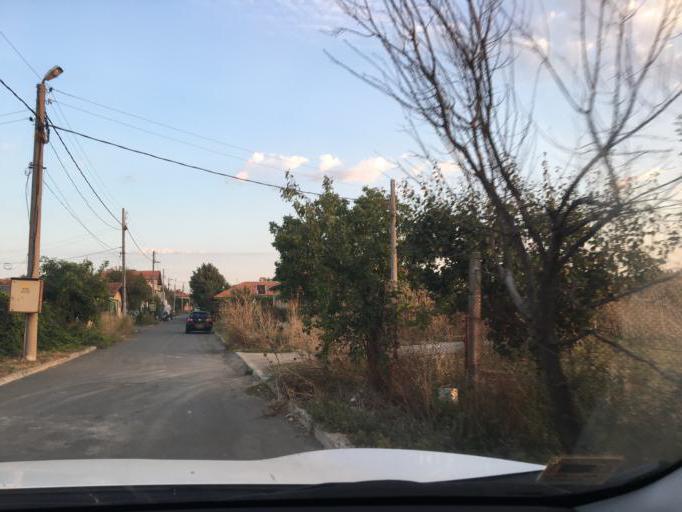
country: BG
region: Burgas
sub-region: Obshtina Burgas
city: Burgas
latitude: 42.6115
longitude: 27.4968
